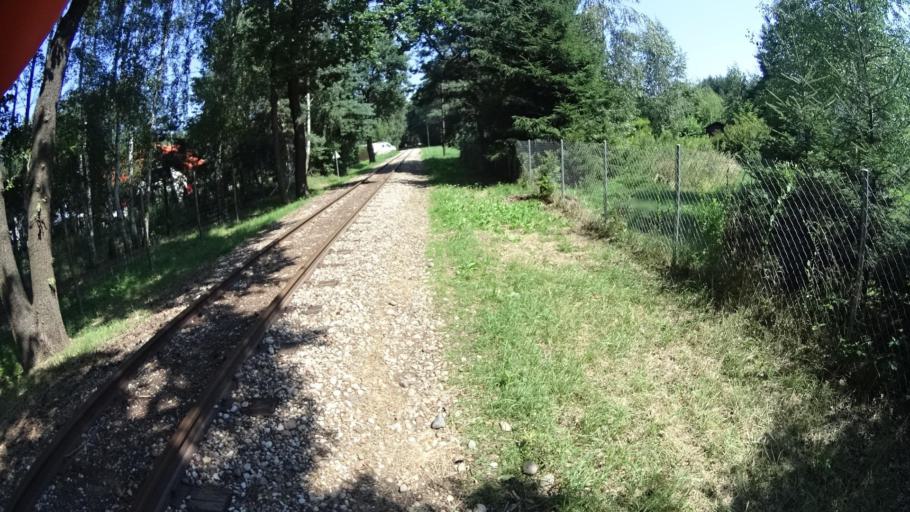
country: PL
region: Masovian Voivodeship
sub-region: Powiat piaseczynski
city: Tarczyn
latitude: 51.9929
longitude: 20.8926
